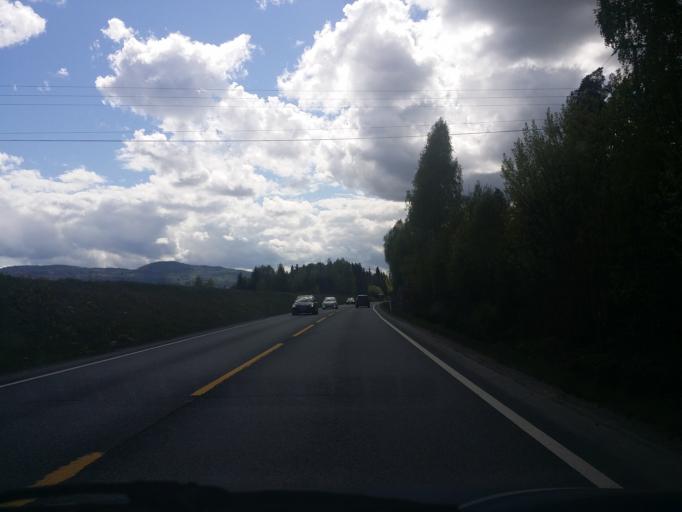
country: NO
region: Buskerud
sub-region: Modum
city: Vikersund
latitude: 59.9589
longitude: 9.9783
